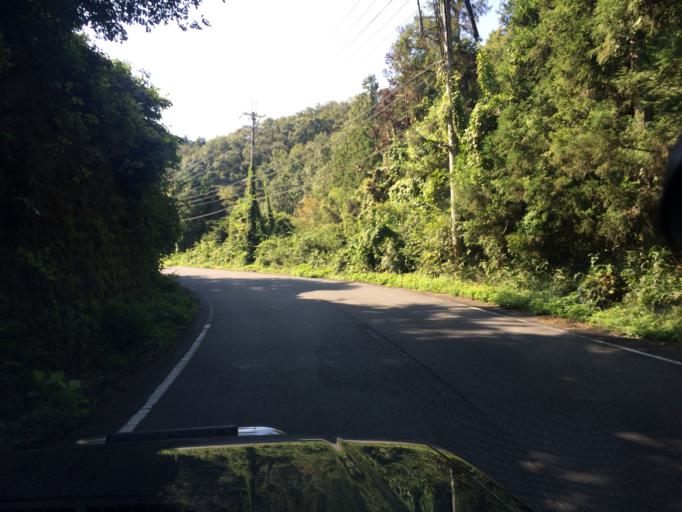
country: JP
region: Mie
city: Ueno-ebisumachi
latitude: 34.7351
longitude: 135.9756
